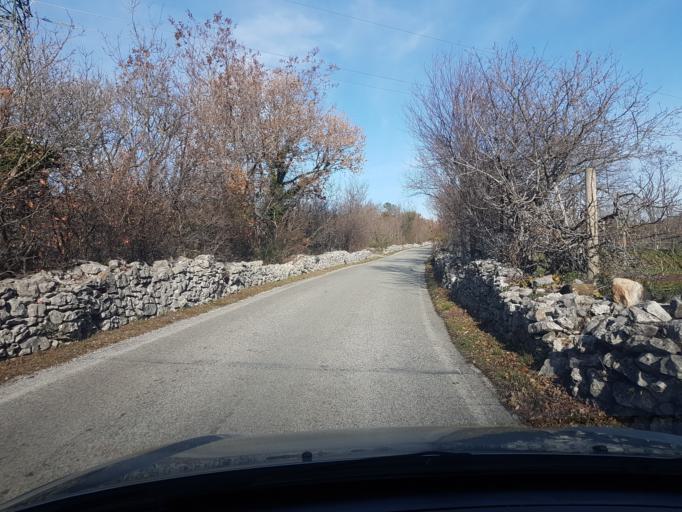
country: IT
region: Friuli Venezia Giulia
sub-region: Provincia di Trieste
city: Sistiana-Visogliano
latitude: 45.7801
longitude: 13.6397
